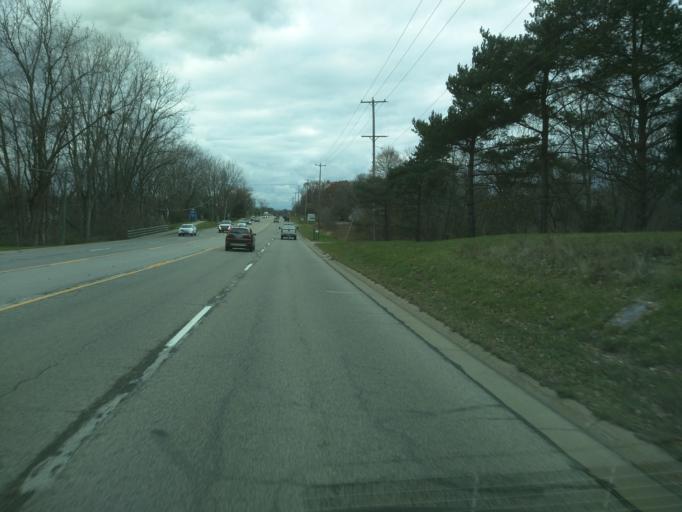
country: US
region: Michigan
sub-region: Ingham County
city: Okemos
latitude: 42.7160
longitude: -84.4004
